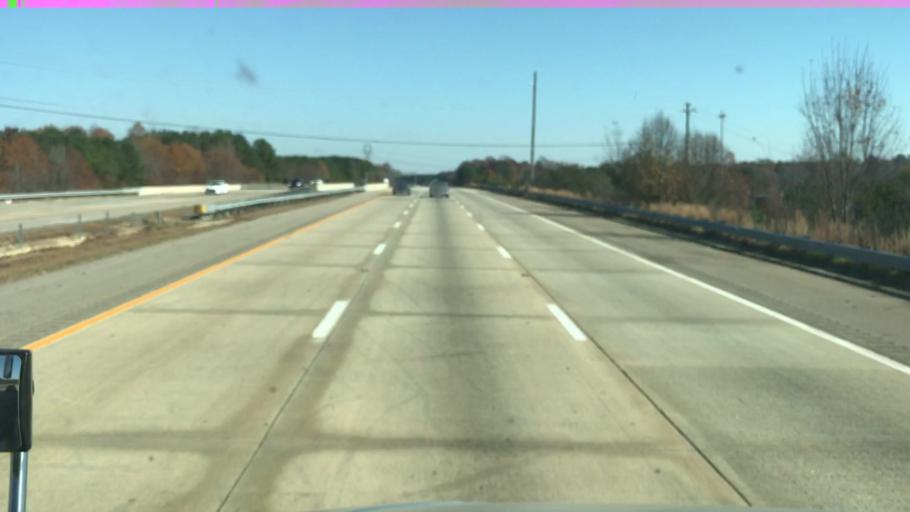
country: US
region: North Carolina
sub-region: Wake County
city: Knightdale
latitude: 35.7671
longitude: -78.4666
